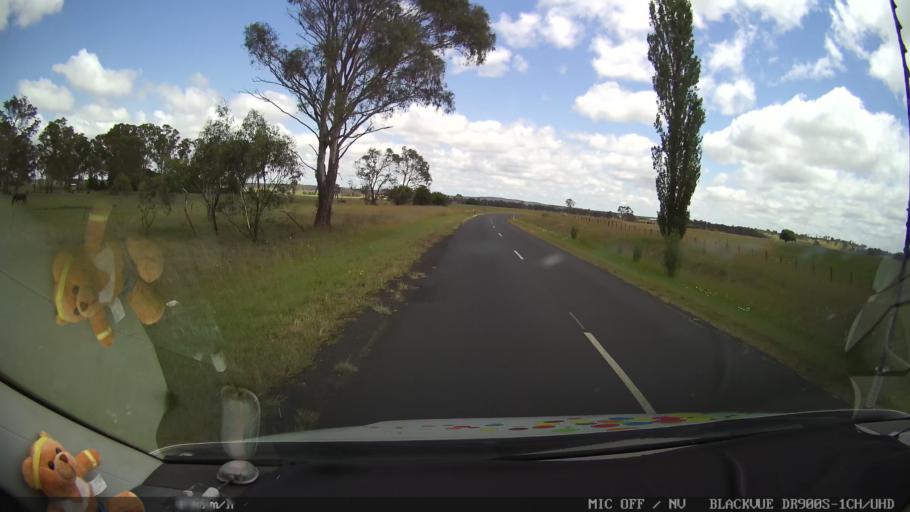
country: AU
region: New South Wales
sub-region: Glen Innes Severn
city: Glen Innes
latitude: -29.6614
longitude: 151.6926
